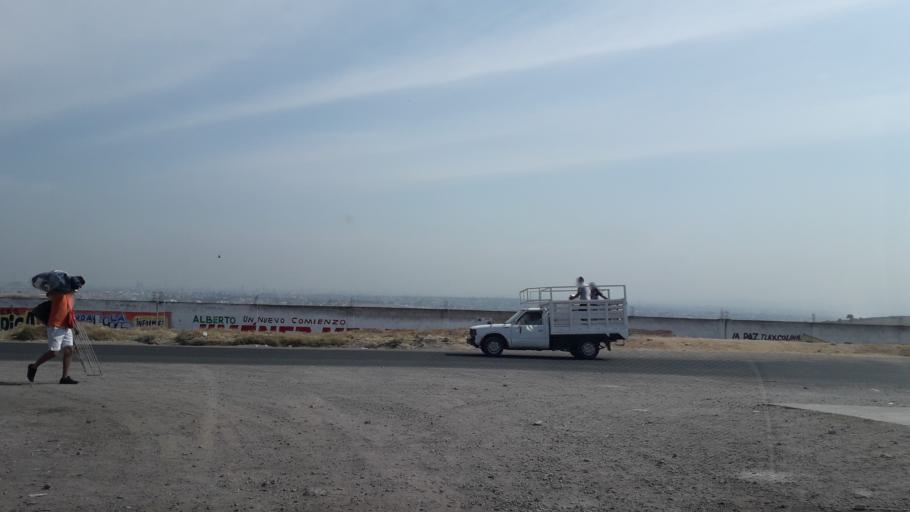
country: MX
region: Puebla
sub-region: Puebla
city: El Capulo (La Quebradora)
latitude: 18.9350
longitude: -98.2666
